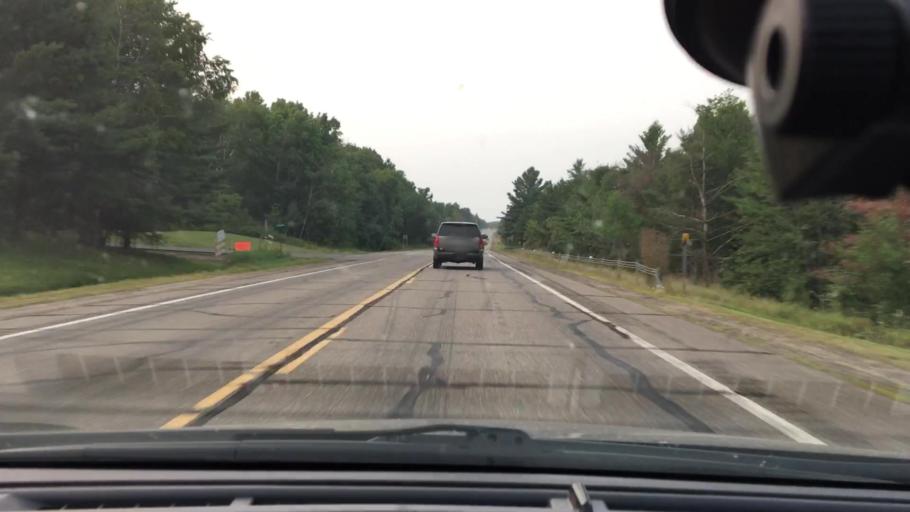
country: US
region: Minnesota
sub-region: Crow Wing County
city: Crosby
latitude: 46.4167
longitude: -93.8729
